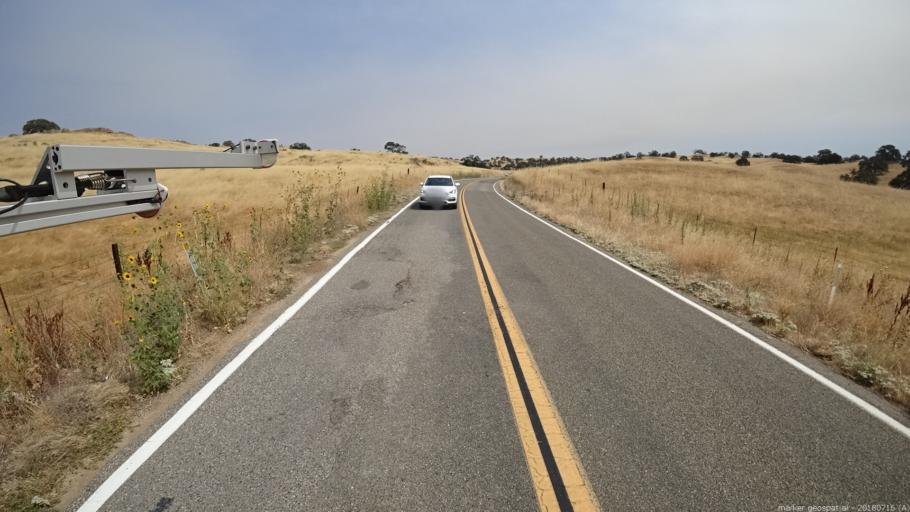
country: US
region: California
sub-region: Madera County
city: Yosemite Lakes
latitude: 37.1366
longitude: -119.9176
